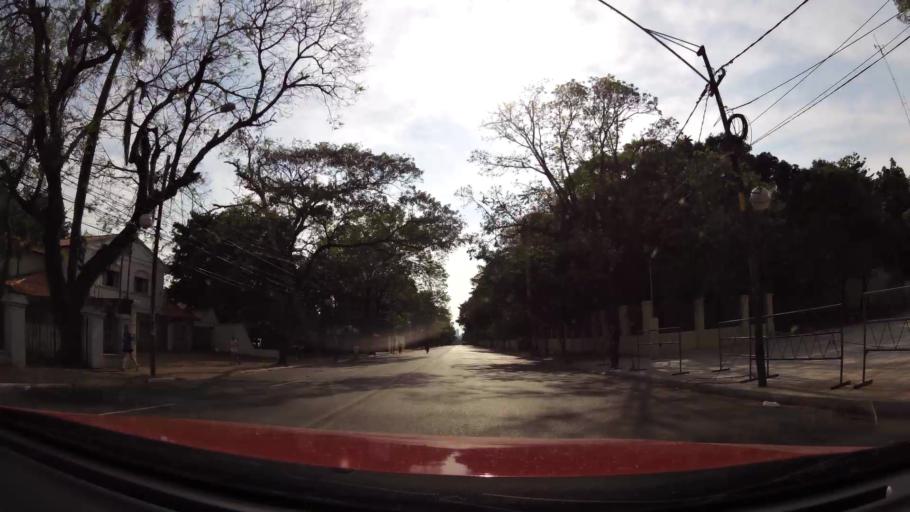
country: PY
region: Asuncion
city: Asuncion
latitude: -25.2924
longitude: -57.6026
